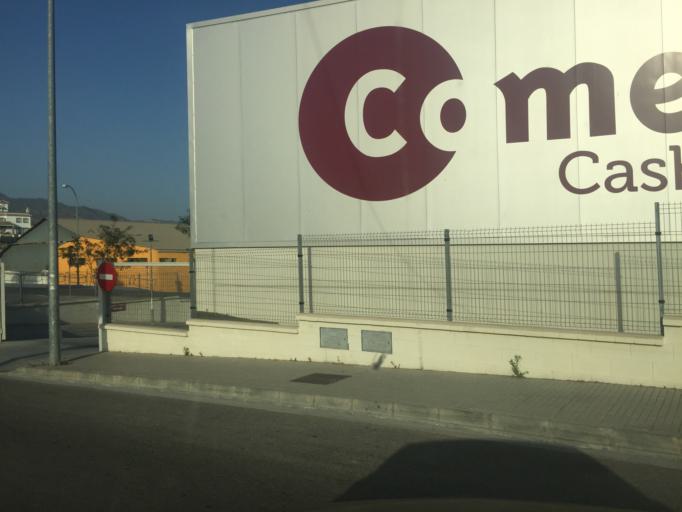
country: ES
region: Andalusia
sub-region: Provincia de Malaga
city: Nerja
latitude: 36.7541
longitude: -3.8847
